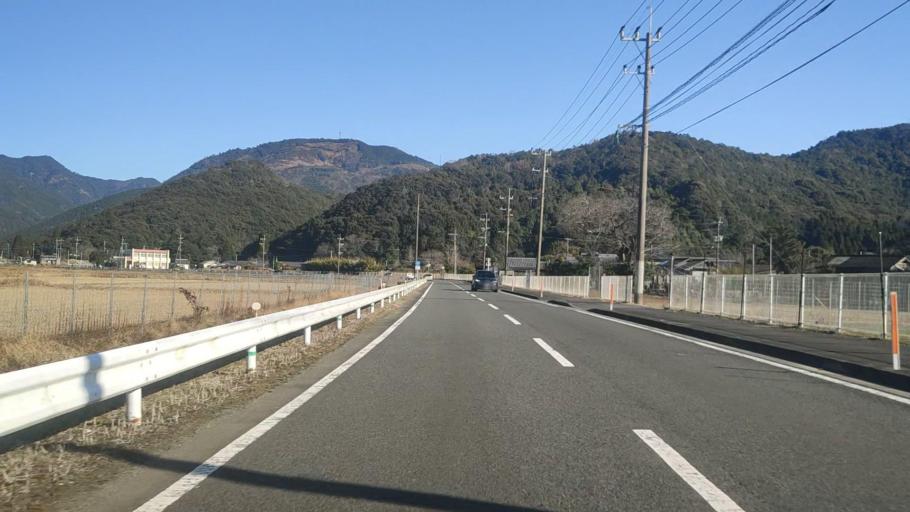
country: JP
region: Miyazaki
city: Nobeoka
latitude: 32.6801
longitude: 131.7864
